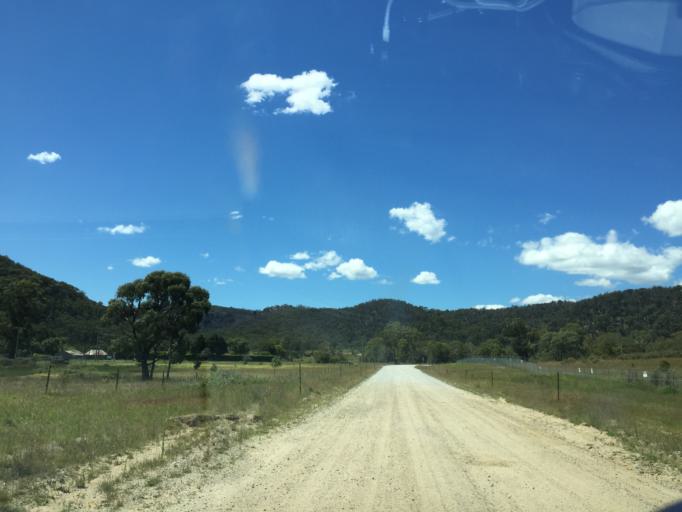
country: AU
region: New South Wales
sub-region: Lithgow
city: Lithgow
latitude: -33.4333
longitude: 150.1338
